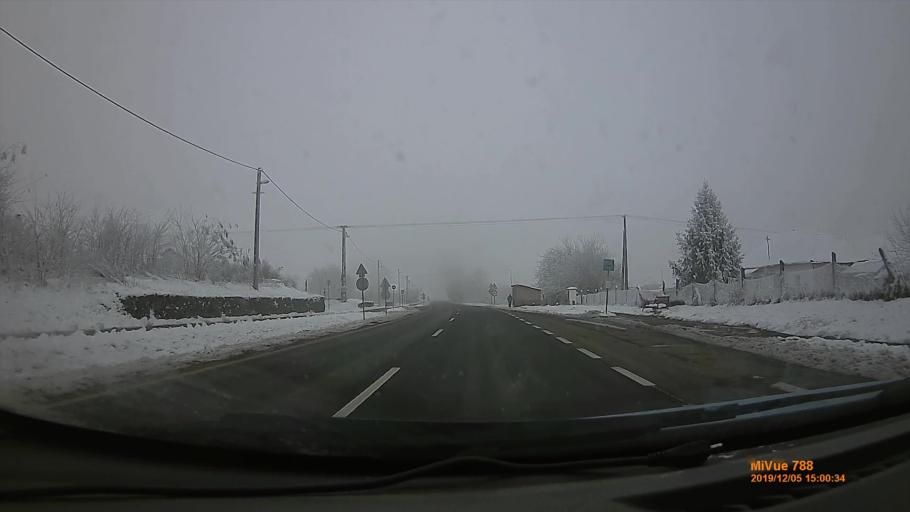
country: HU
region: Szabolcs-Szatmar-Bereg
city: Tiszanagyfalu
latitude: 48.0647
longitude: 21.5386
